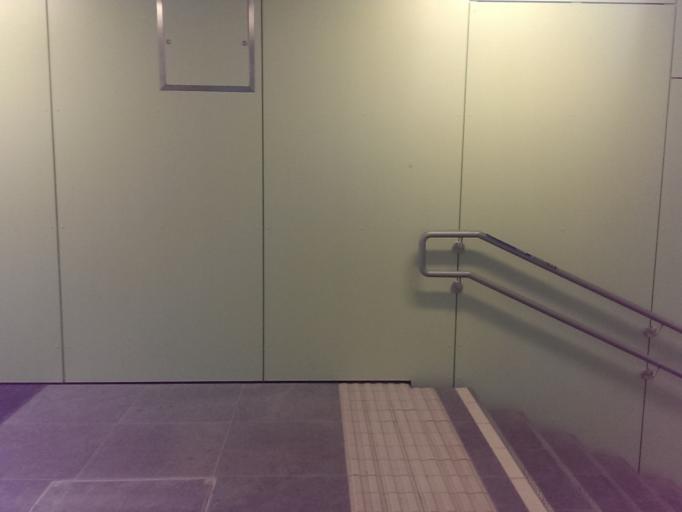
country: AT
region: Styria
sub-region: Politischer Bezirk Bruck-Muerzzuschlag
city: Muerzzuschlag
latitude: 47.6076
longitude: 15.6771
